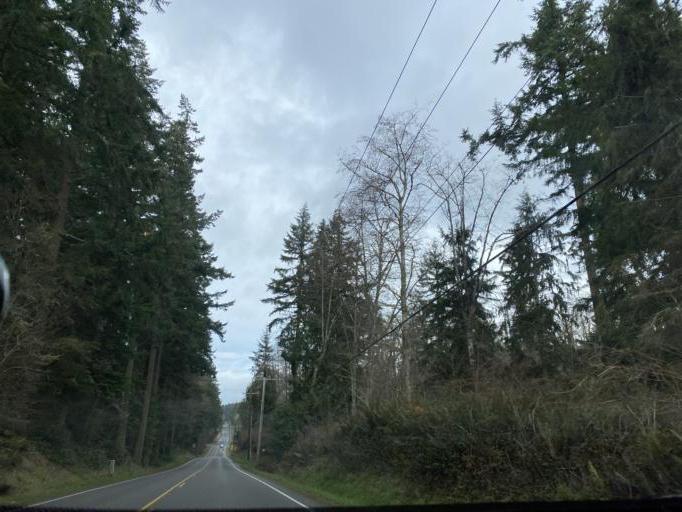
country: US
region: Washington
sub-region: Island County
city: Freeland
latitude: 48.0627
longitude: -122.5067
